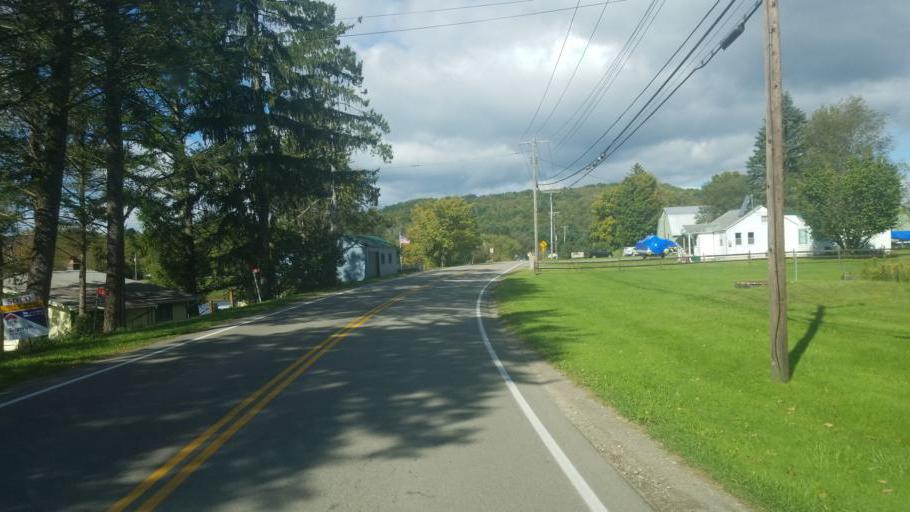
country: US
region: New York
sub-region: Allegany County
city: Cuba
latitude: 42.2596
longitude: -78.2959
